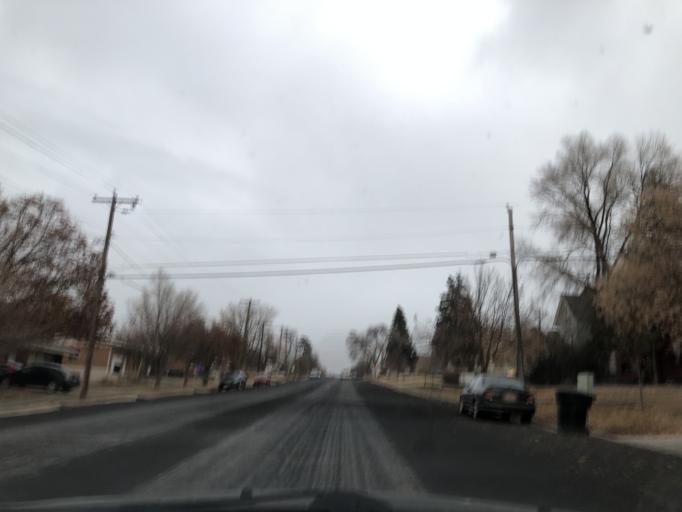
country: US
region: Utah
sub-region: Cache County
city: Logan
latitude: 41.7370
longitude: -111.8262
